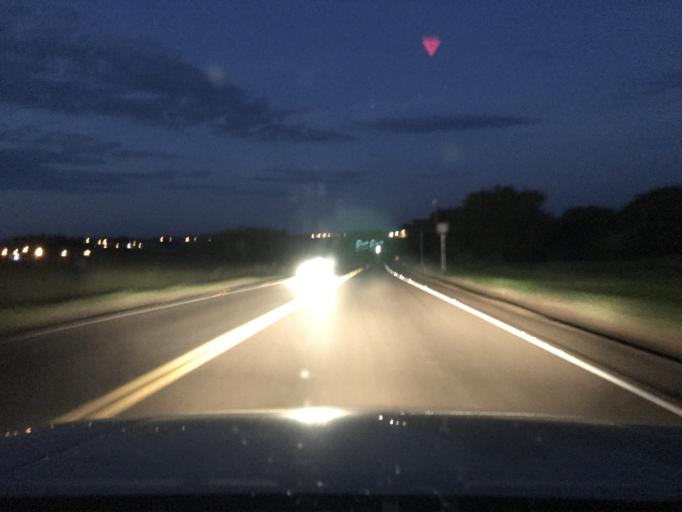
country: PY
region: Canindeyu
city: Salto del Guaira
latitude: -24.1060
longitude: -54.2381
